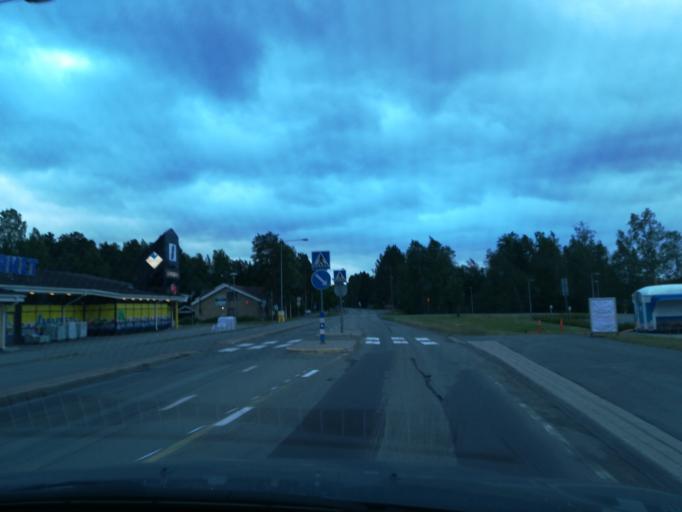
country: FI
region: Southern Savonia
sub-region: Mikkeli
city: Ristiina
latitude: 61.5112
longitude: 27.2465
